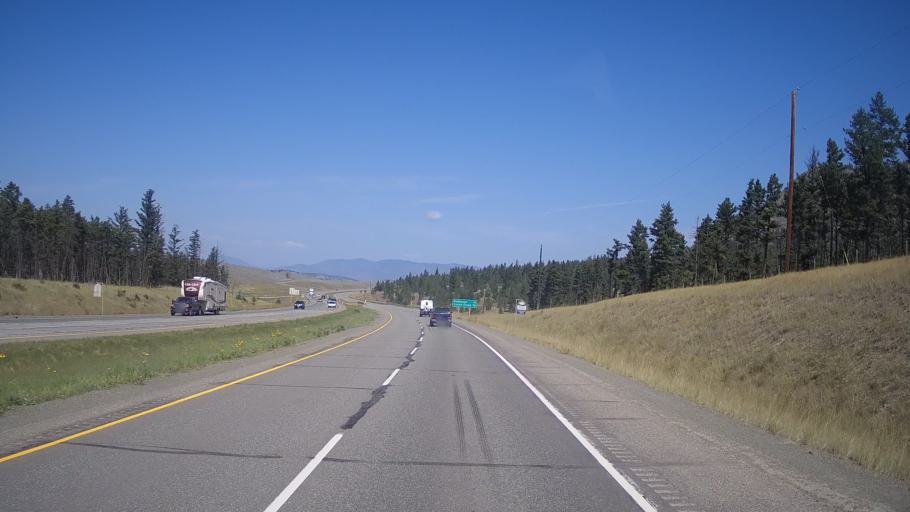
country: CA
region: British Columbia
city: Kamloops
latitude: 50.6246
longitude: -120.4728
